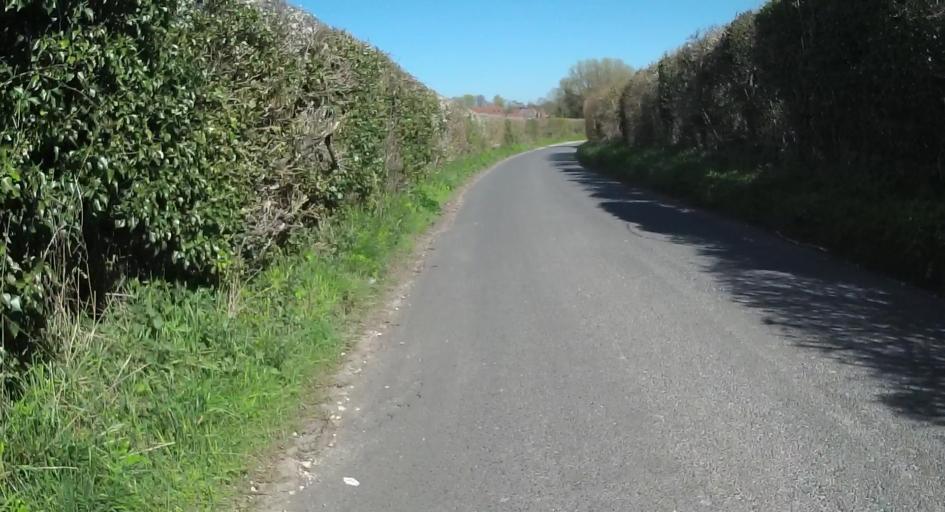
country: GB
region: England
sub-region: Hampshire
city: Hook
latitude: 51.2512
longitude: -0.9792
